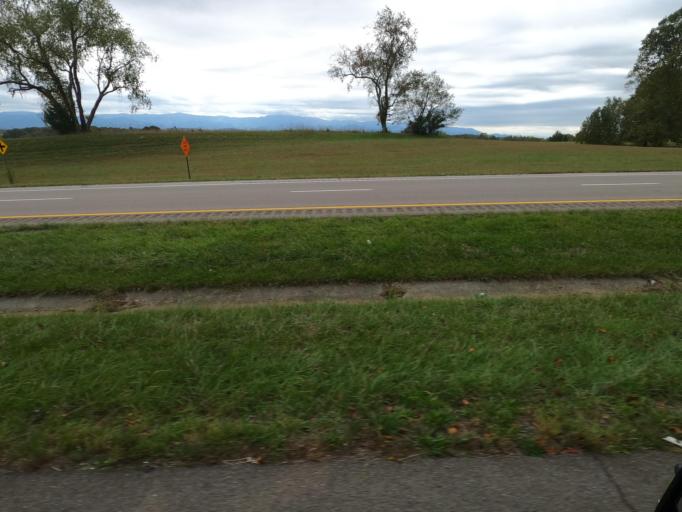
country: US
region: Tennessee
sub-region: Greene County
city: Tusculum
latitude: 36.2314
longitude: -82.6455
